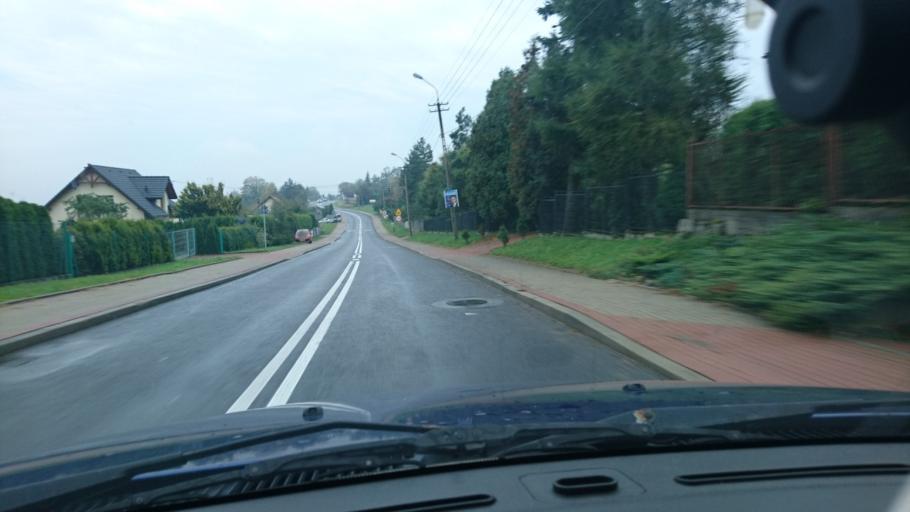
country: PL
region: Silesian Voivodeship
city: Janowice
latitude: 49.8411
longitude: 19.1010
